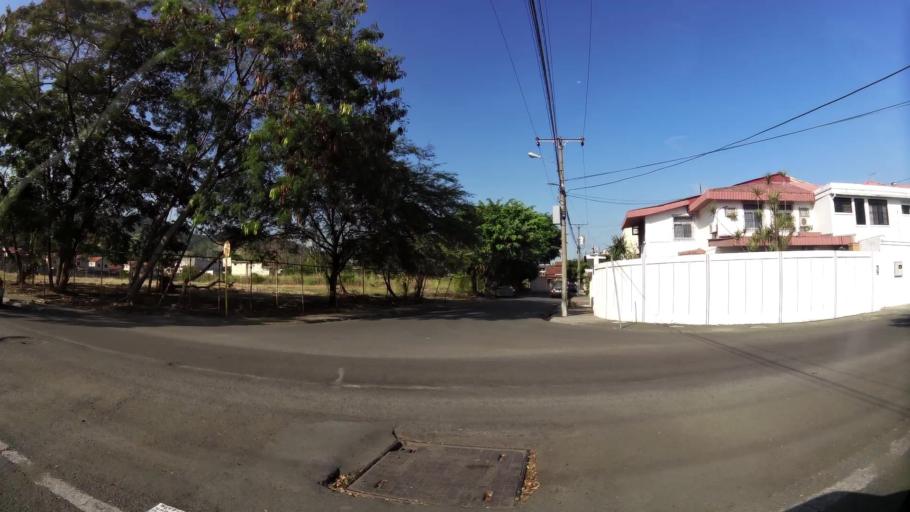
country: EC
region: Guayas
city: Santa Lucia
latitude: -2.1900
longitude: -79.9628
